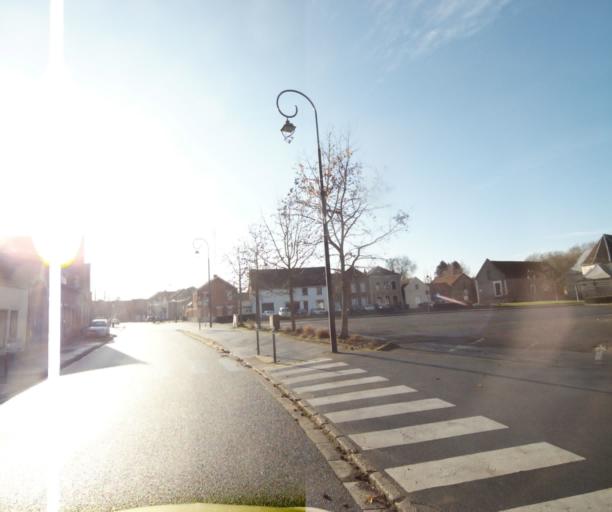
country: FR
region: Nord-Pas-de-Calais
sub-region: Departement du Nord
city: Maing
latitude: 50.3062
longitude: 3.4794
